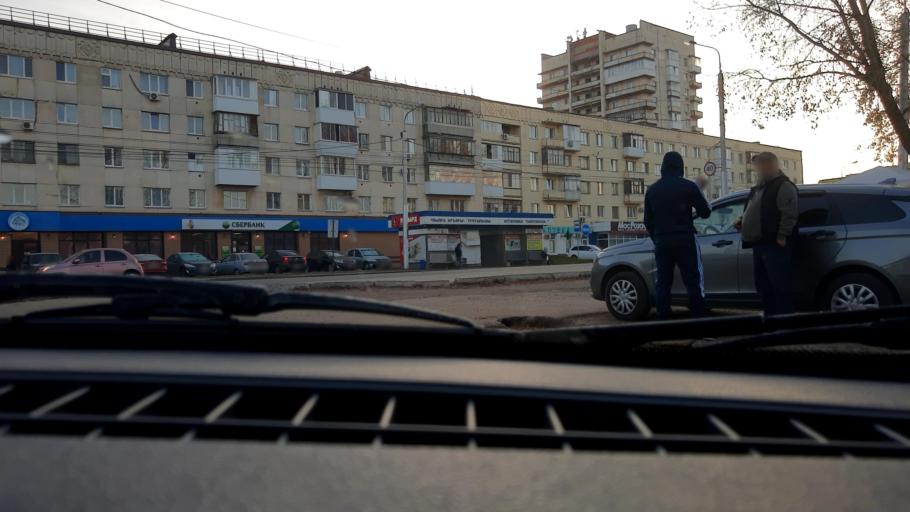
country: RU
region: Bashkortostan
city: Mikhaylovka
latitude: 54.7893
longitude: 55.8806
